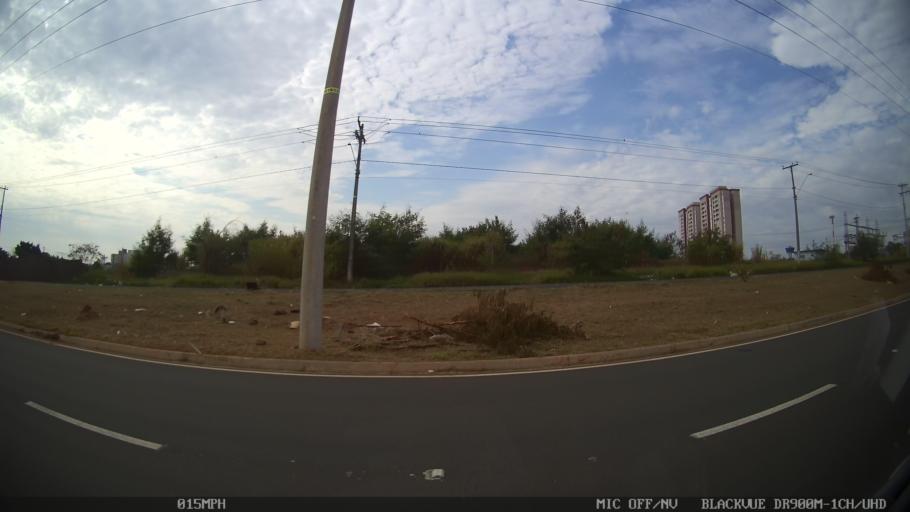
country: BR
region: Sao Paulo
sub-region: Americana
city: Americana
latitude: -22.7620
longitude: -47.3447
